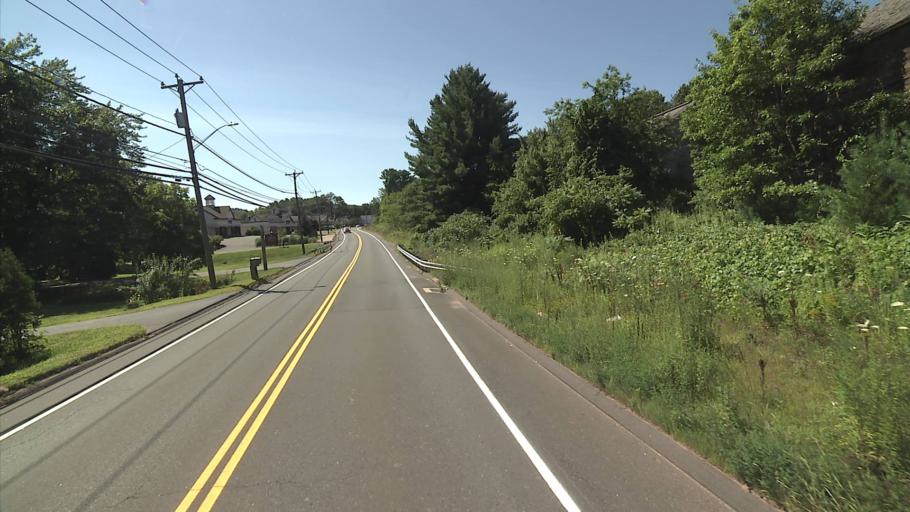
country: US
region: Connecticut
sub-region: Hartford County
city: Tariffville
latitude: 41.9058
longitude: -72.7871
